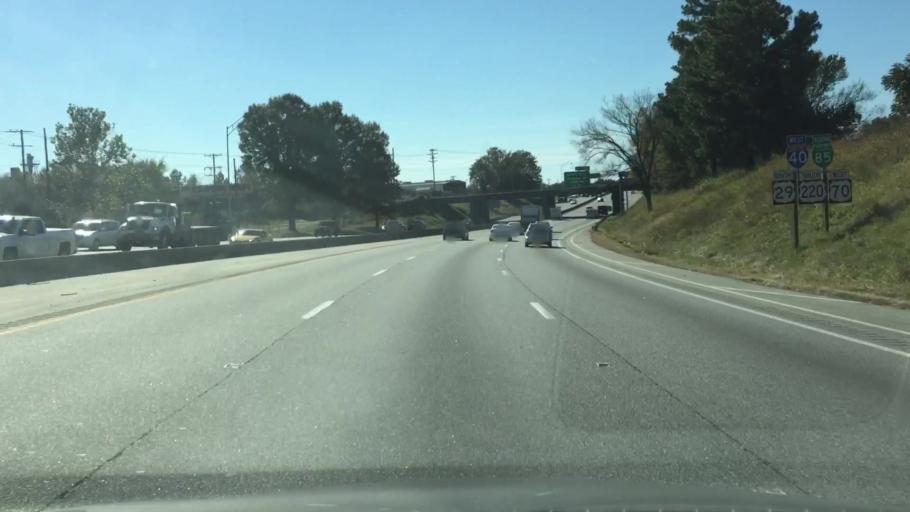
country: US
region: North Carolina
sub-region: Guilford County
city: Greensboro
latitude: 36.0397
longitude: -79.7802
